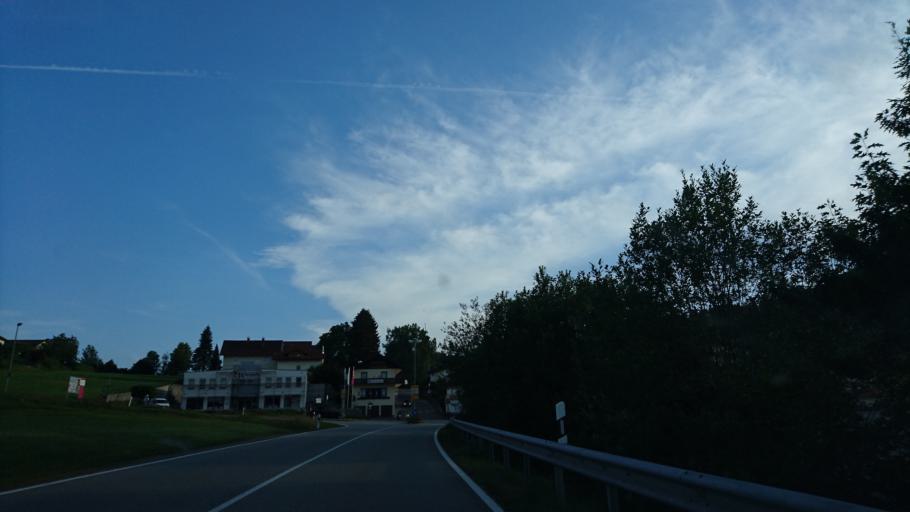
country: DE
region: Bavaria
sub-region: Lower Bavaria
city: Grafenau
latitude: 48.8516
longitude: 13.3947
